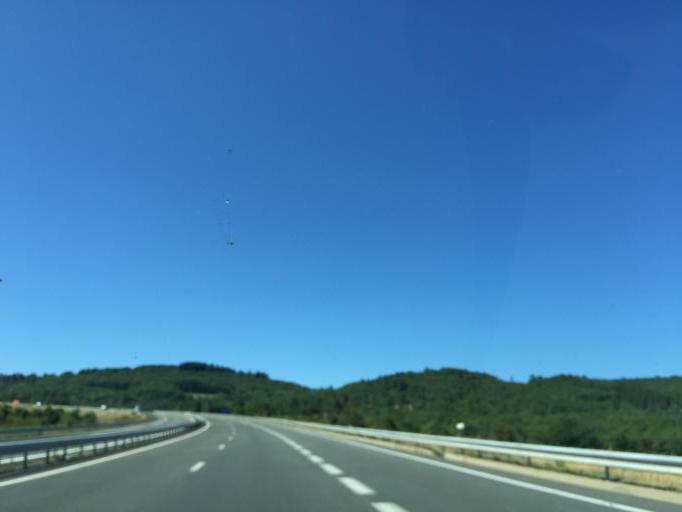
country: FR
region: Midi-Pyrenees
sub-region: Departement de l'Aveyron
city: La Cavalerie
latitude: 43.9696
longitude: 3.2087
